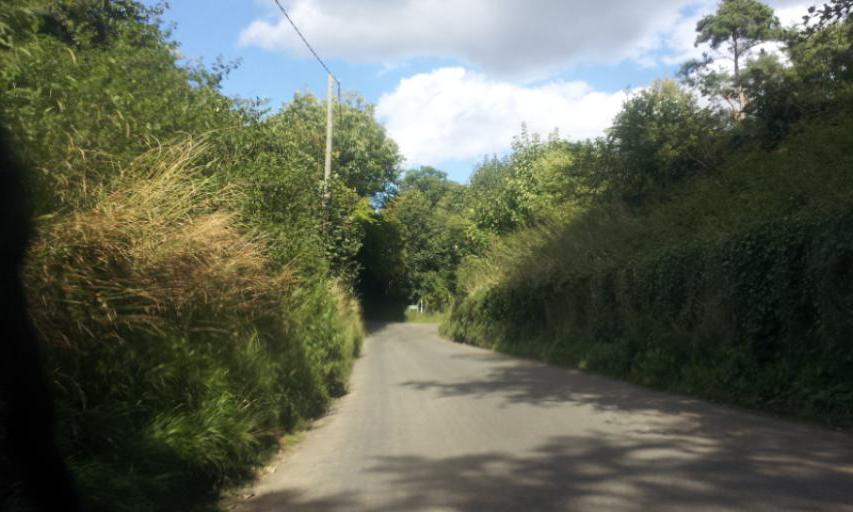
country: GB
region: England
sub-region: Kent
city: West Malling
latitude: 51.3223
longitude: 0.4122
